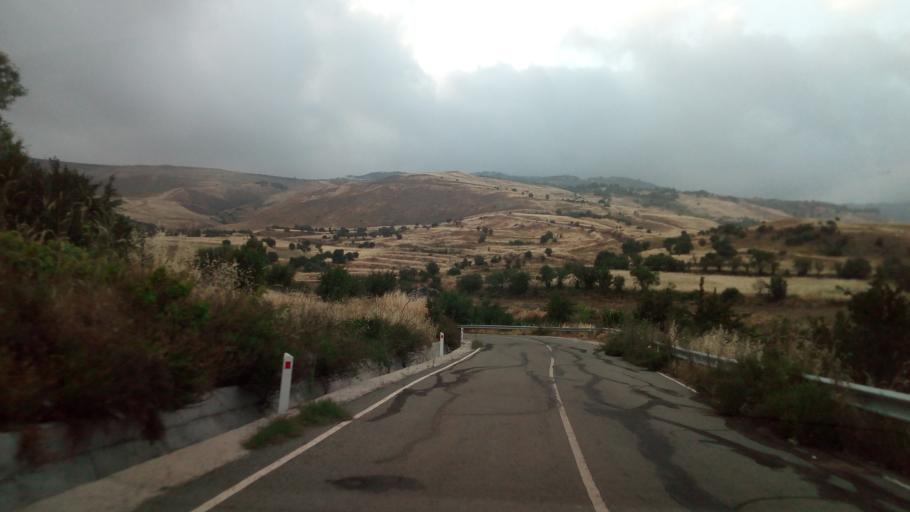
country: CY
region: Limassol
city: Pachna
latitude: 34.8665
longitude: 32.6388
